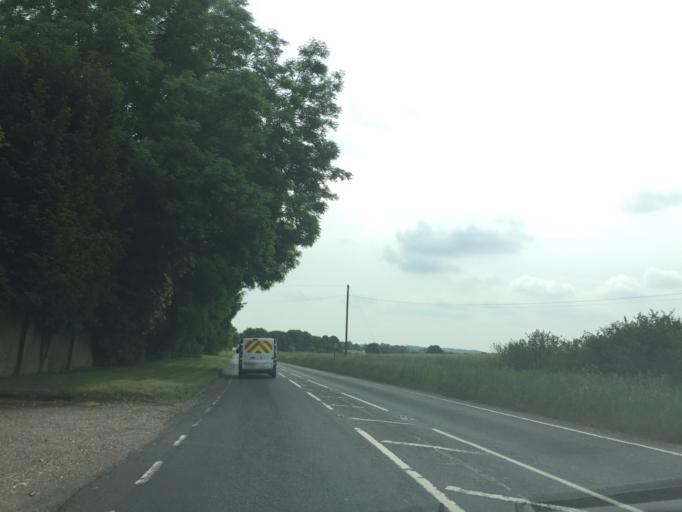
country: GB
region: England
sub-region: Hampshire
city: Four Marks
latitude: 51.0957
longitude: -1.0817
